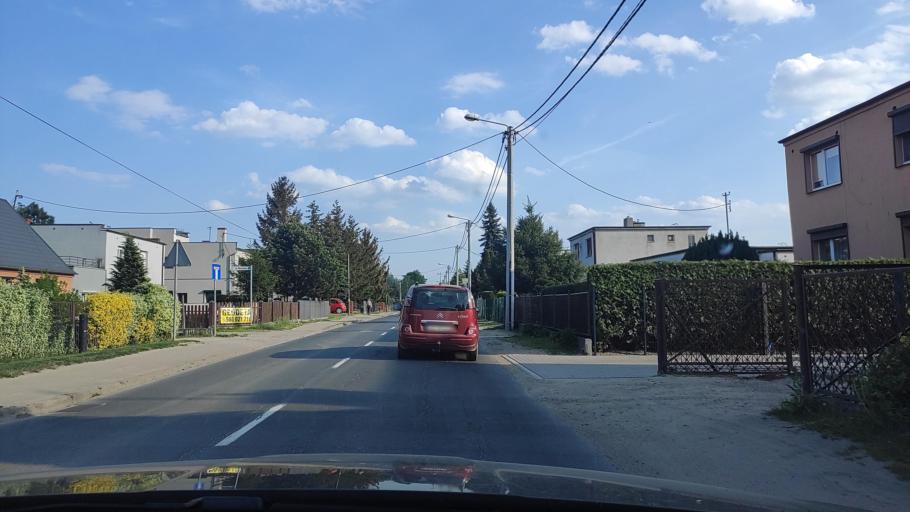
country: PL
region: Greater Poland Voivodeship
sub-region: Powiat poznanski
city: Kleszczewo
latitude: 52.3876
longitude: 17.1595
